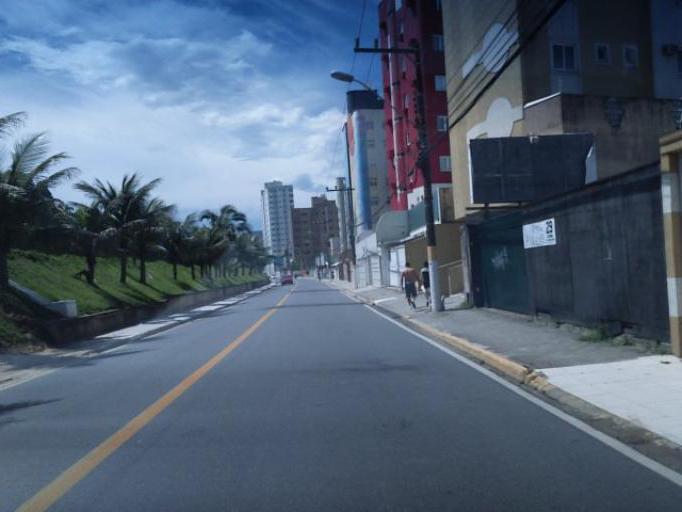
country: BR
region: Santa Catarina
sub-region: Itapema
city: Itapema
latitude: -27.1126
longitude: -48.6103
